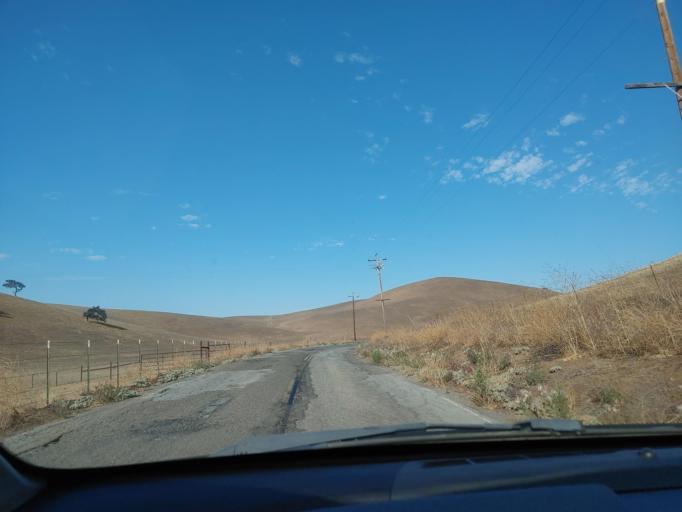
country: US
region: California
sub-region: San Benito County
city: Ridgemark
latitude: 36.7992
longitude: -121.2813
